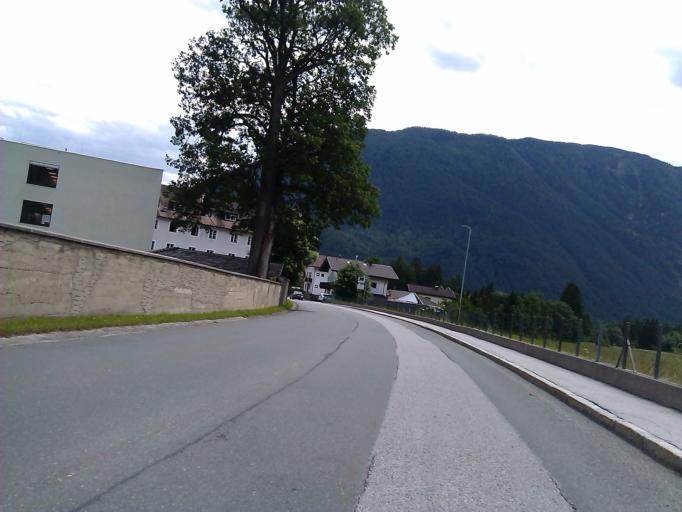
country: AT
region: Tyrol
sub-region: Politischer Bezirk Imst
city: Nassereith
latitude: 47.3161
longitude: 10.8338
